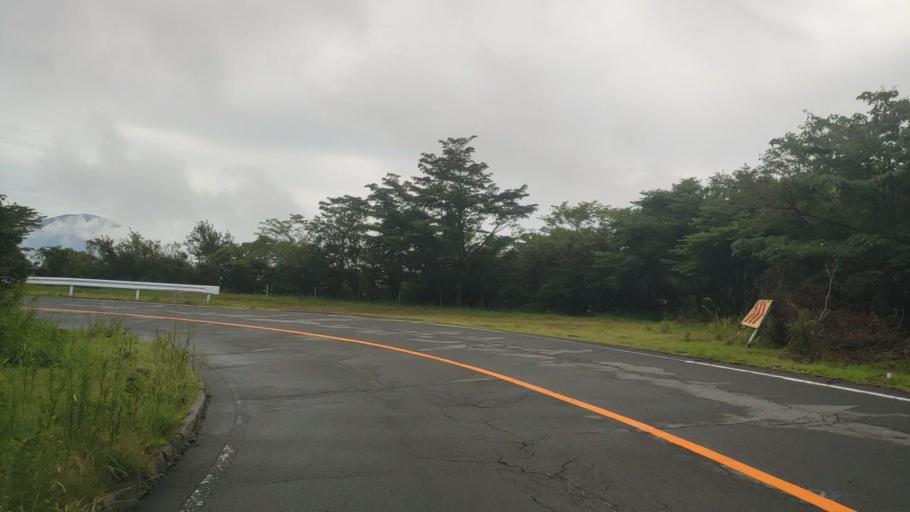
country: JP
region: Shizuoka
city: Fuji
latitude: 35.2908
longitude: 138.7758
